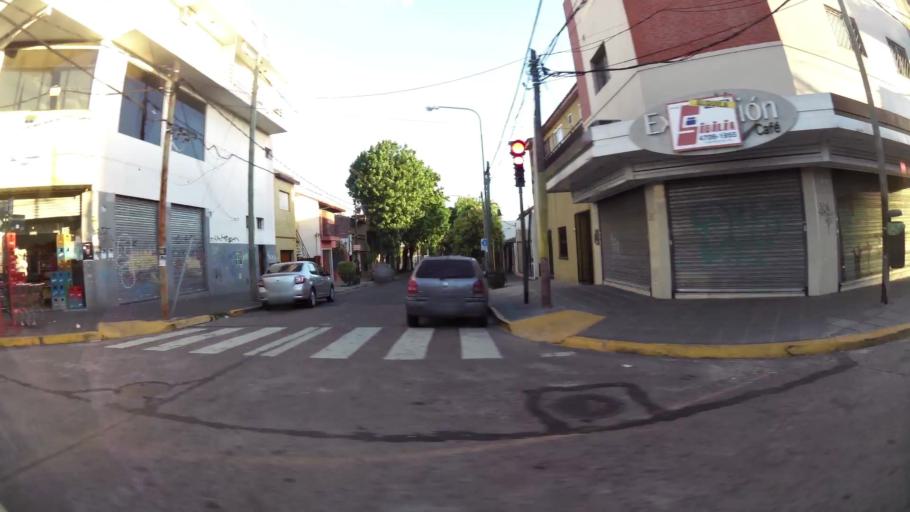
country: AR
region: Buenos Aires
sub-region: Partido de General San Martin
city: General San Martin
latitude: -34.5506
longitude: -58.5100
